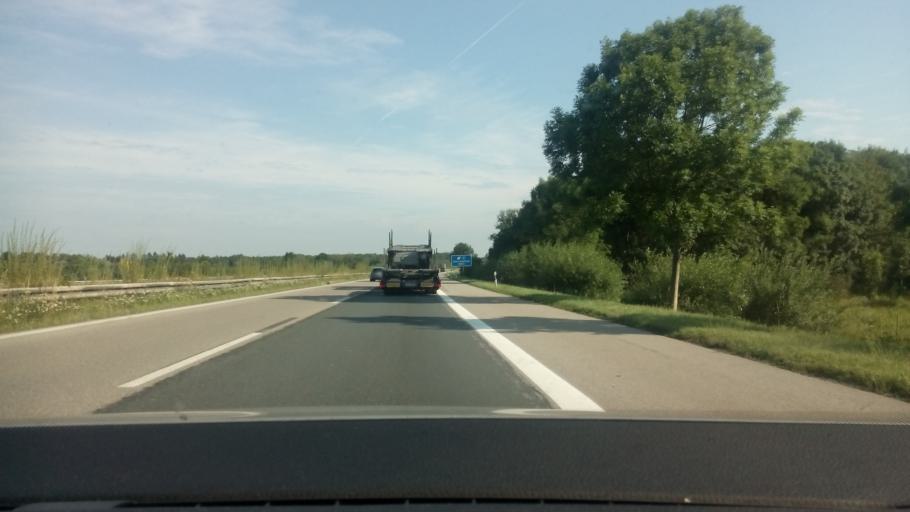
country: DE
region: Bavaria
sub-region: Upper Bavaria
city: Oberschleissheim
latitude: 48.2408
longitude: 11.5358
